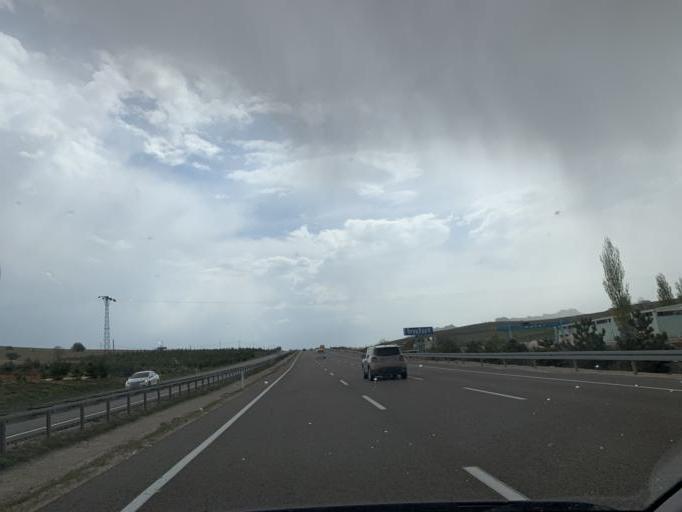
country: TR
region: Eskisehir
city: Sivrihisar
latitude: 39.4809
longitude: 31.5959
